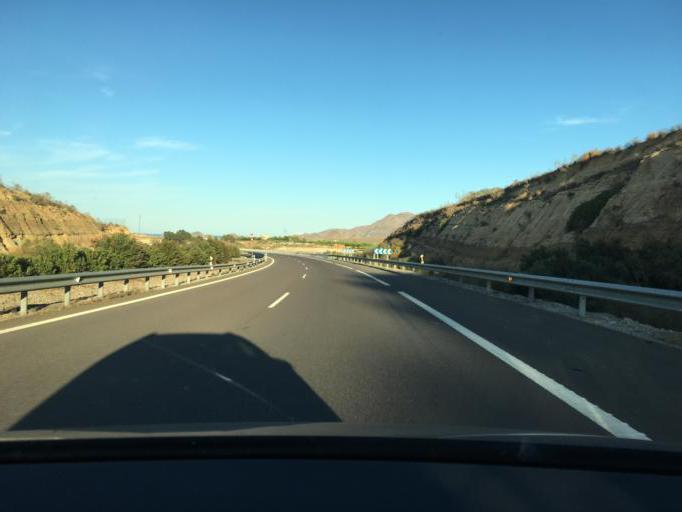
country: ES
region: Andalusia
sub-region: Provincia de Almeria
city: Bedar
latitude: 37.1453
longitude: -1.9665
